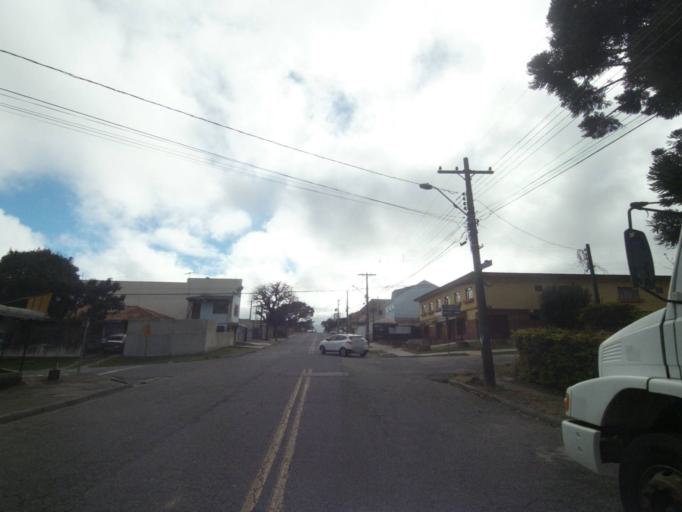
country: BR
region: Parana
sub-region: Sao Jose Dos Pinhais
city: Sao Jose dos Pinhais
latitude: -25.5258
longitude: -49.3017
